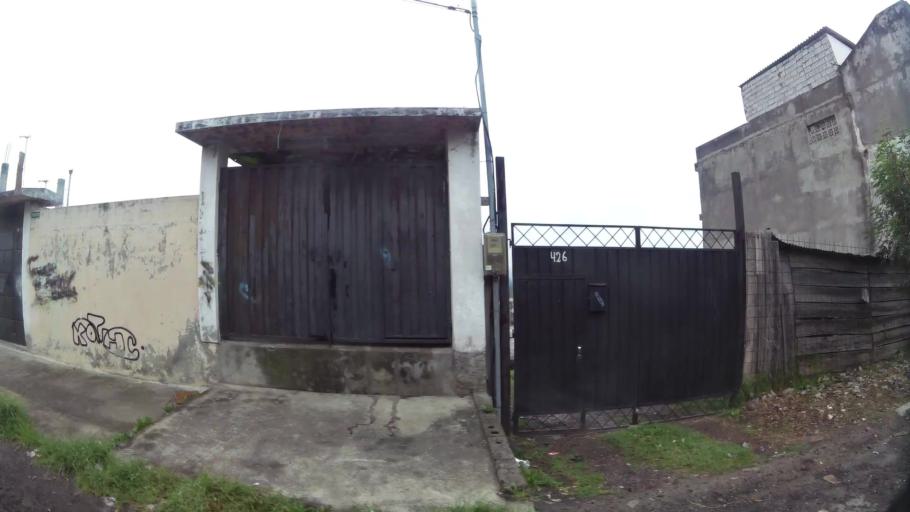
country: EC
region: Pichincha
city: Sangolqui
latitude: -0.2768
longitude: -78.4699
